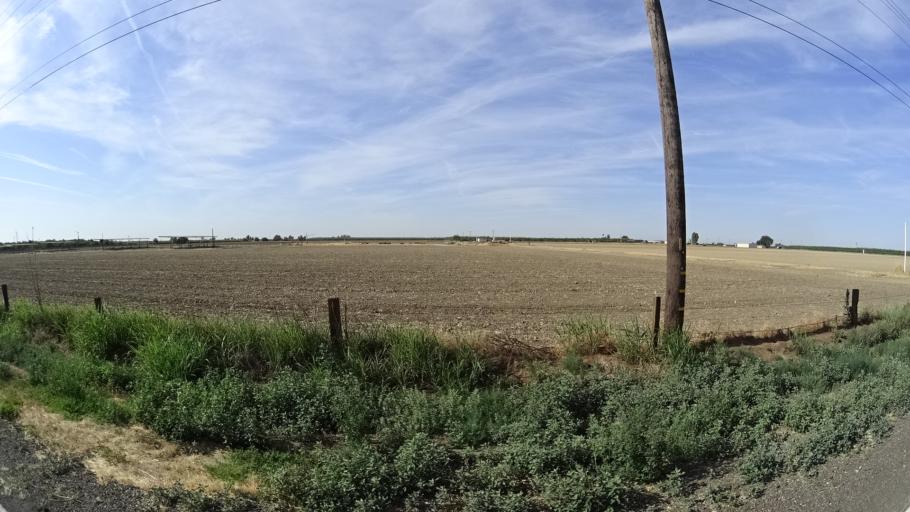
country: US
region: California
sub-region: Tulare County
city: Goshen
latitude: 36.3425
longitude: -119.4882
